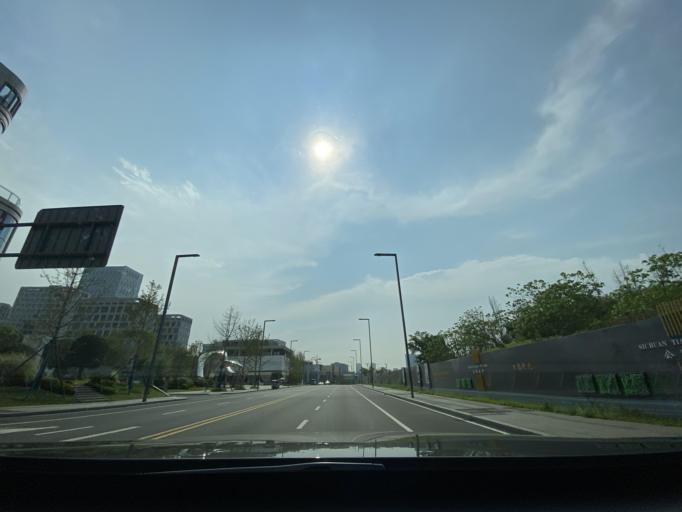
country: CN
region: Sichuan
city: Dongsheng
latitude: 30.3927
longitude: 104.0866
